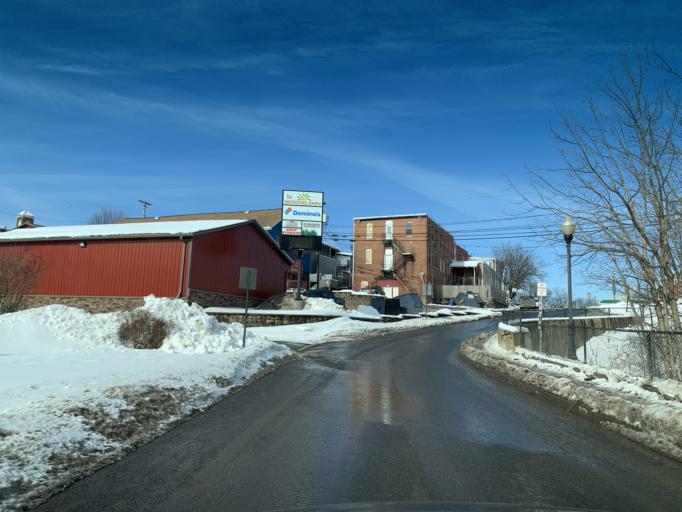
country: US
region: Maryland
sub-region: Allegany County
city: Frostburg
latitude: 39.6549
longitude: -78.9260
